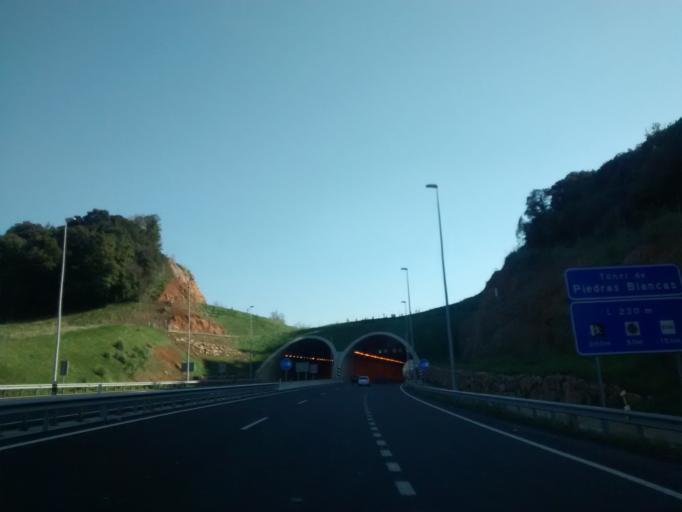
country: ES
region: Cantabria
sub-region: Provincia de Cantabria
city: Camargo
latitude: 43.4151
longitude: -3.8720
